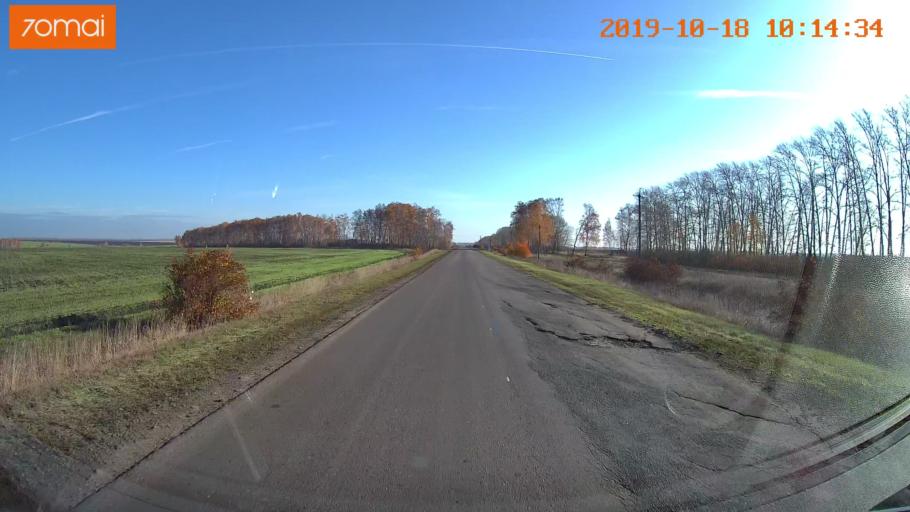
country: RU
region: Tula
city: Kurkino
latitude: 53.4052
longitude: 38.5461
